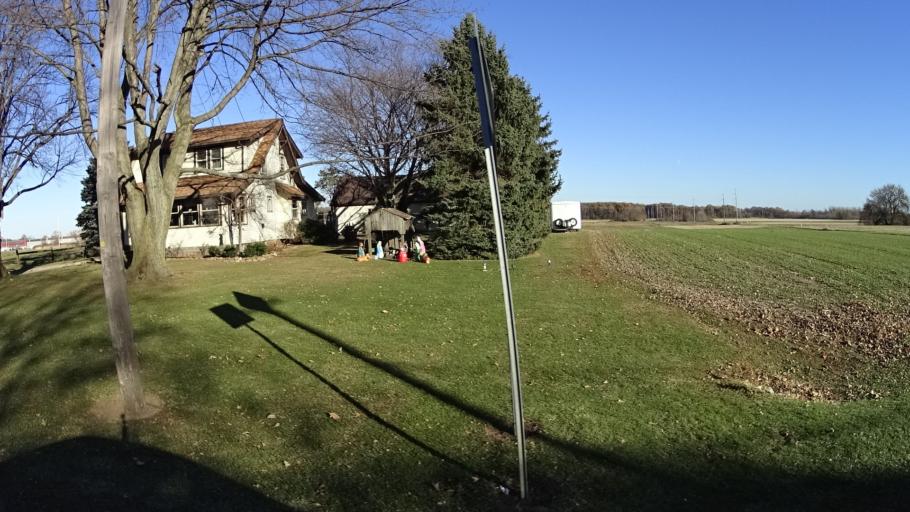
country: US
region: Ohio
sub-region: Lorain County
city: Elyria
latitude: 41.3658
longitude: -82.1453
